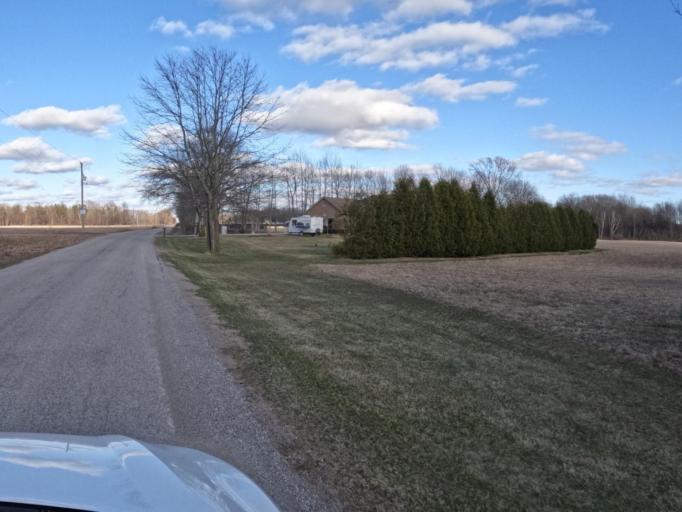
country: CA
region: Ontario
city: Norfolk County
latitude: 42.8153
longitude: -80.5721
